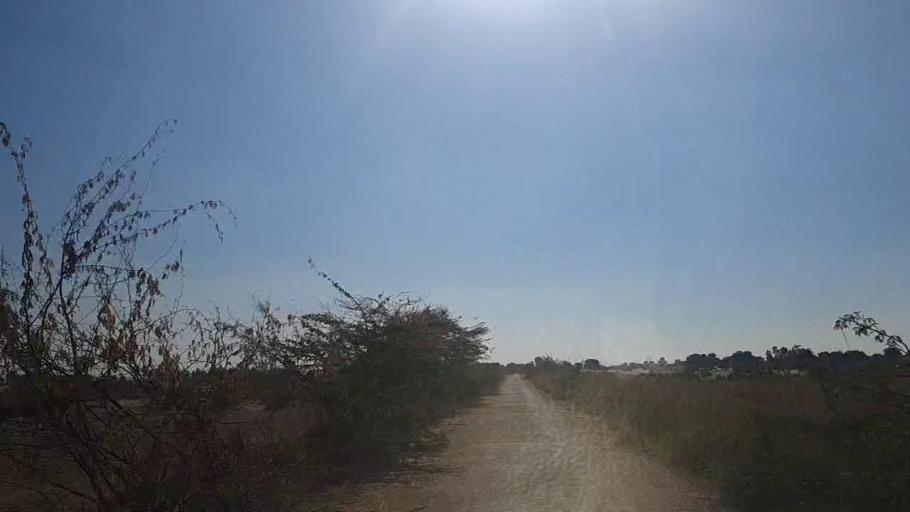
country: PK
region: Sindh
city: Khadro
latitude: 26.1599
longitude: 68.8380
